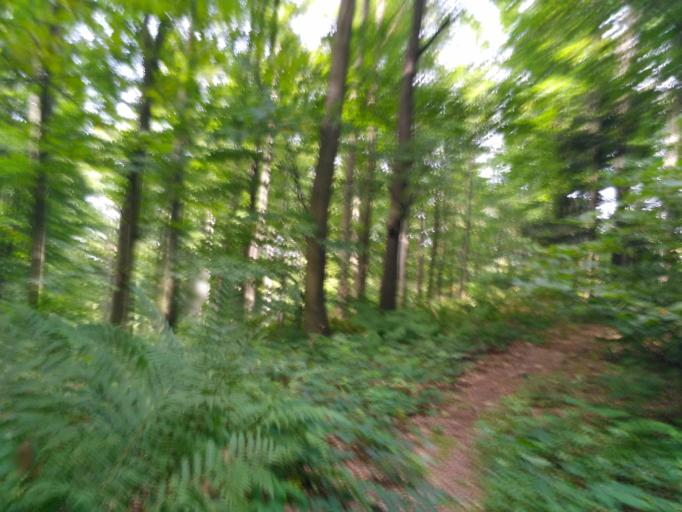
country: PL
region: Subcarpathian Voivodeship
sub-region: Powiat strzyzowski
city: Frysztak
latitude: 49.8891
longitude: 21.5376
